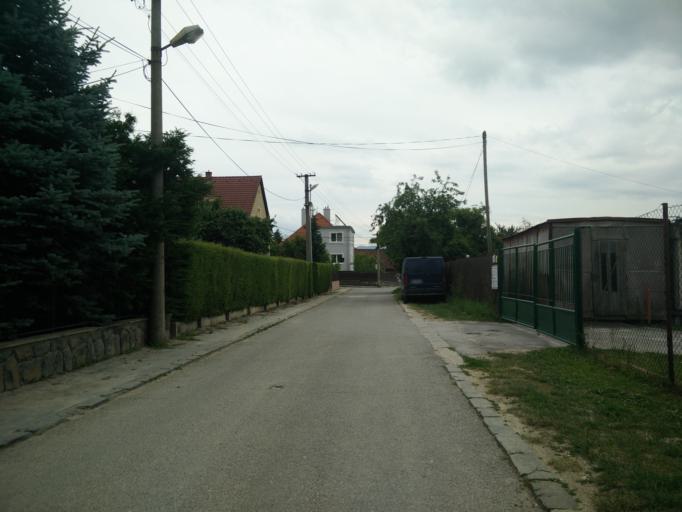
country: SK
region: Nitriansky
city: Bojnice
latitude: 48.7770
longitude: 18.5850
